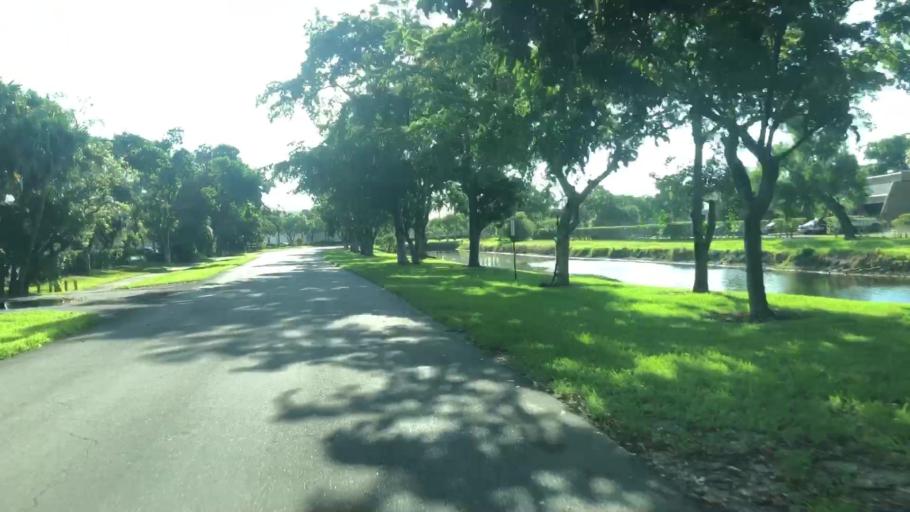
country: US
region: Florida
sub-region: Broward County
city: Kendall Green
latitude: 26.2637
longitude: -80.1432
